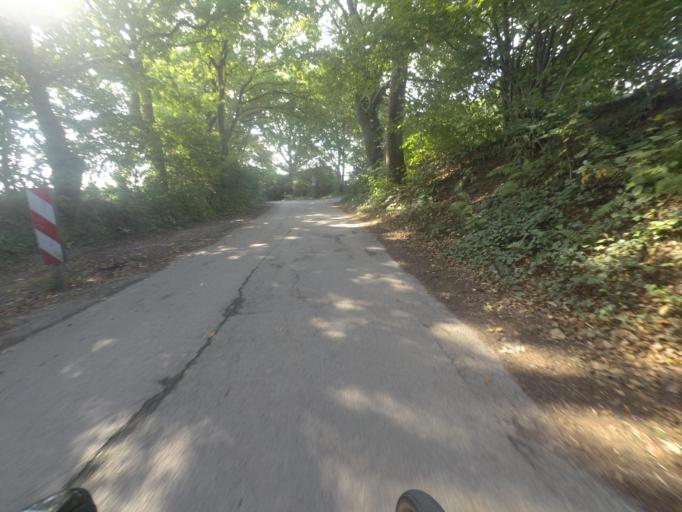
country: DE
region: North Rhine-Westphalia
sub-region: Regierungsbezirk Arnsberg
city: Frondenberg
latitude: 51.4560
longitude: 7.7295
